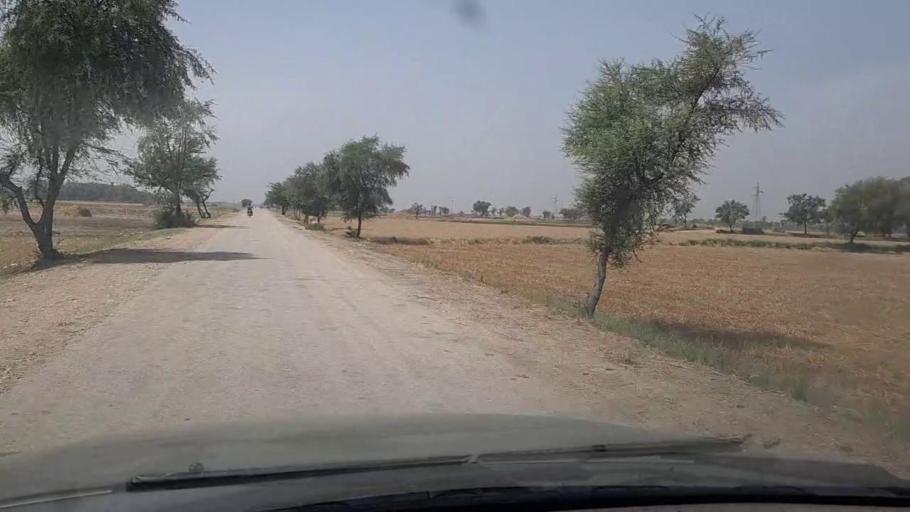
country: PK
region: Sindh
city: Ratodero
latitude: 27.7946
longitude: 68.2439
